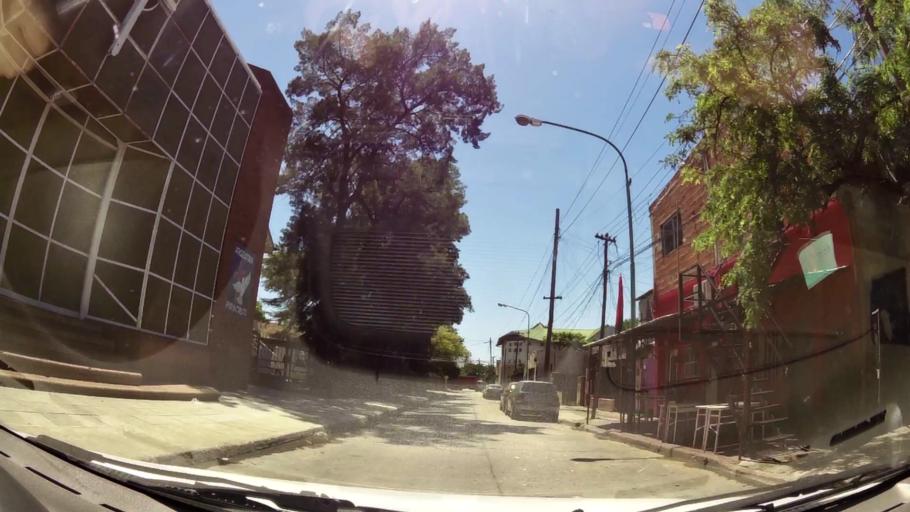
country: AR
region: Buenos Aires
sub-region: Partido de Vicente Lopez
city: Olivos
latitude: -34.5157
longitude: -58.5139
